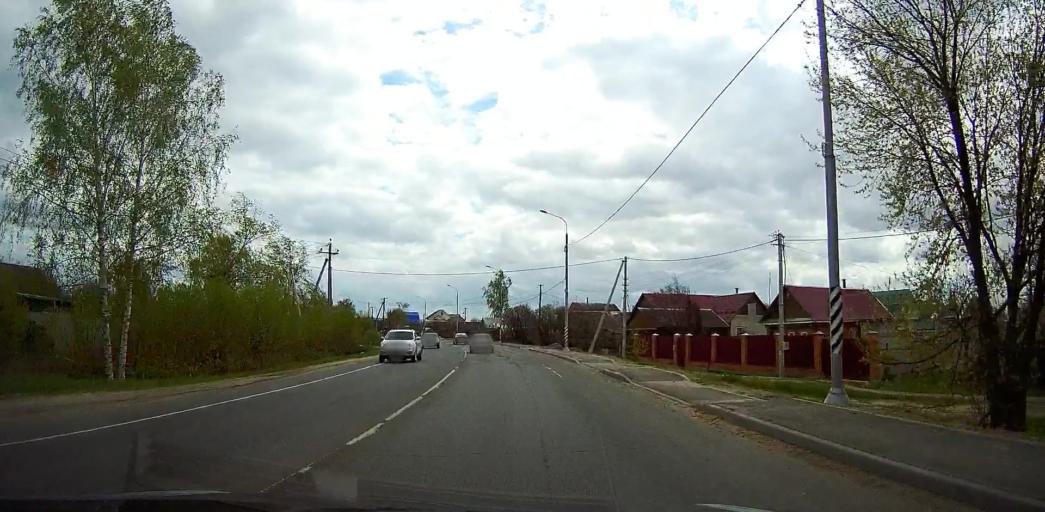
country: RU
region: Moskovskaya
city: Beloozerskiy
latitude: 55.4501
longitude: 38.4408
